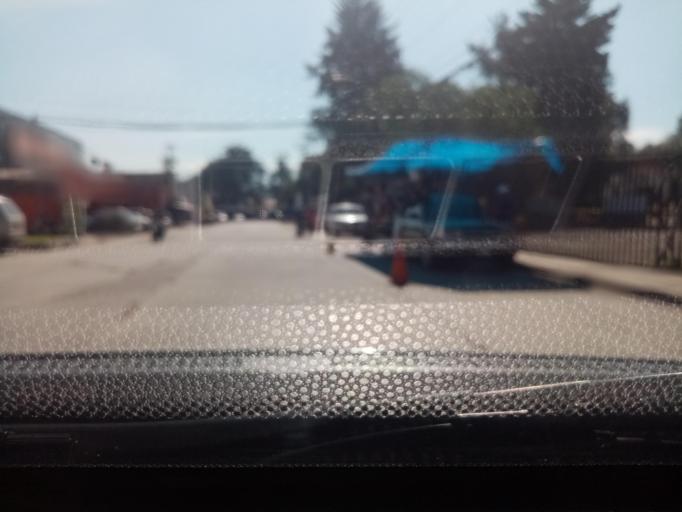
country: GT
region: Quetzaltenango
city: Quetzaltenango
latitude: 14.8491
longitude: -91.5345
